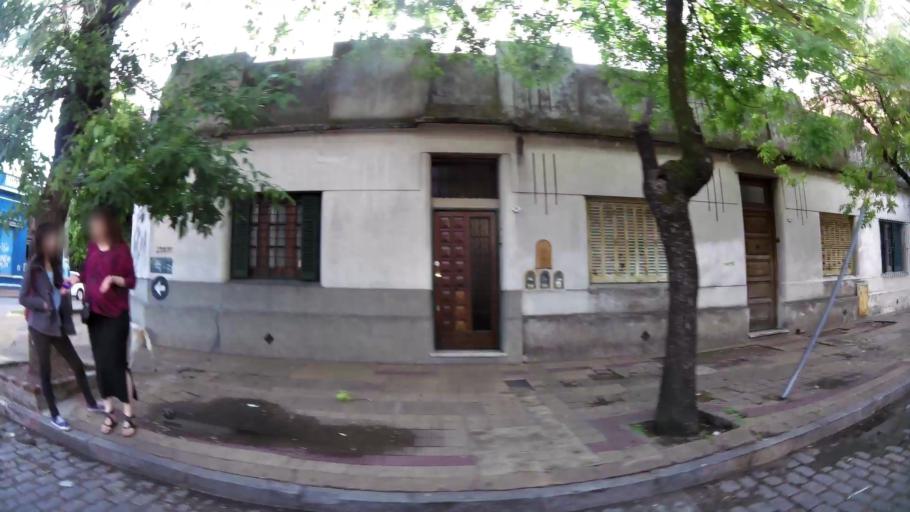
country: AR
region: Buenos Aires
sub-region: Partido de Moron
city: Moron
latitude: -34.6548
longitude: -58.6186
